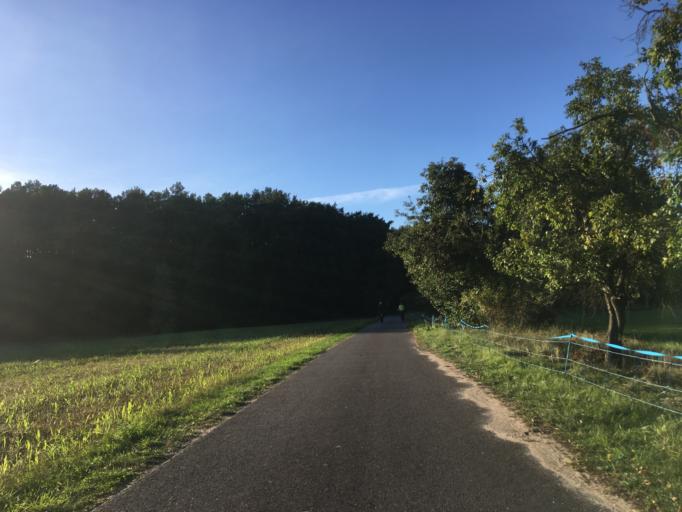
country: PL
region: Lubusz
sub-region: Powiat zarski
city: Trzebiel
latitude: 51.6242
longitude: 14.7558
